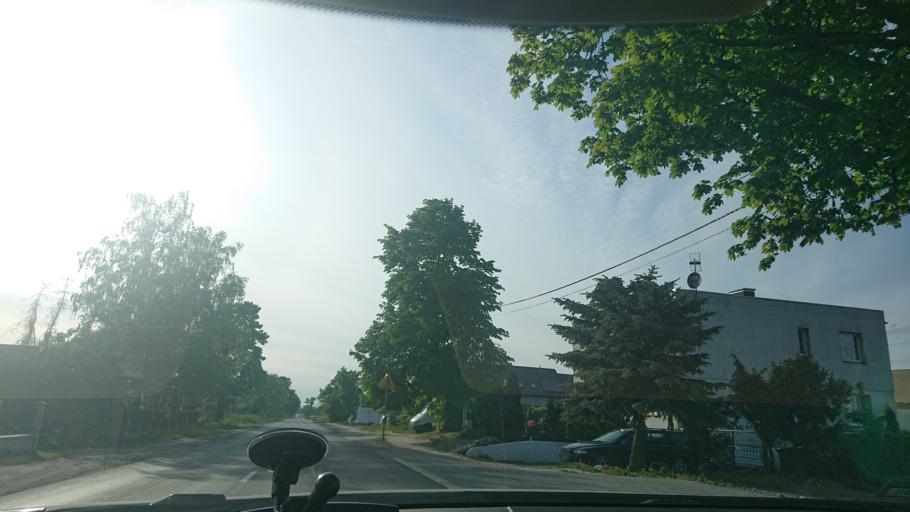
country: PL
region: Greater Poland Voivodeship
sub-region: Powiat gnieznienski
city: Gniezno
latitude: 52.5497
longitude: 17.5562
